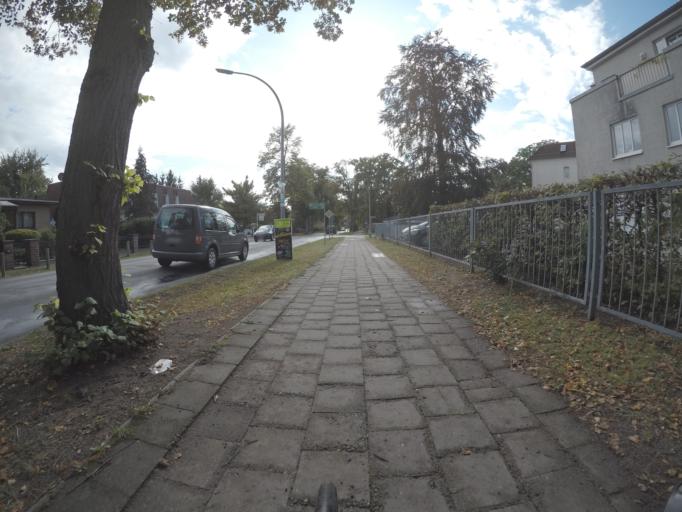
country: DE
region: Brandenburg
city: Strausberg
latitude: 52.5448
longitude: 13.8582
